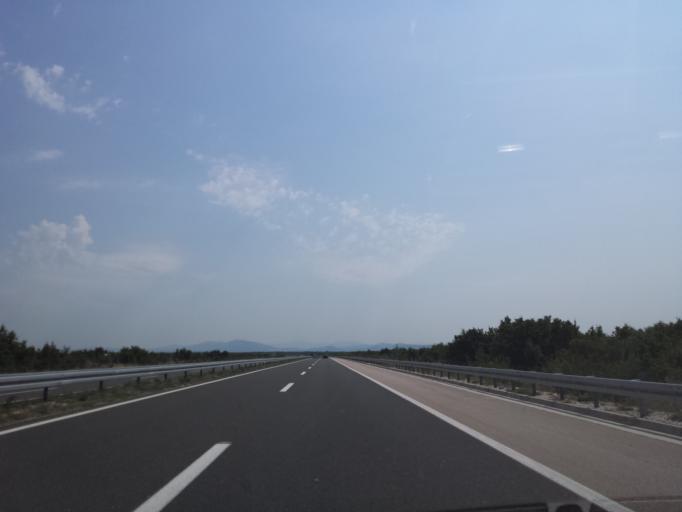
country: HR
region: Sibensko-Kniniska
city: Zaton
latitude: 43.8773
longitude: 15.8011
